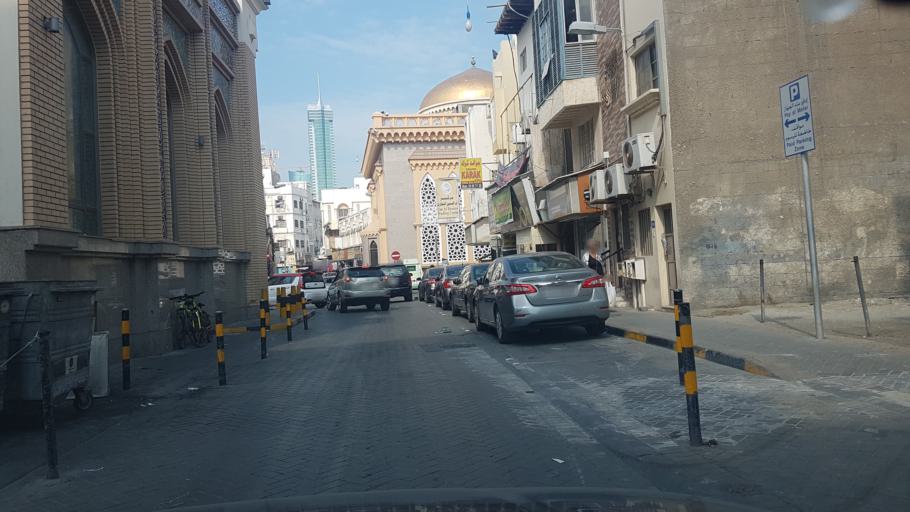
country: BH
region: Manama
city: Manama
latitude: 26.2299
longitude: 50.5778
